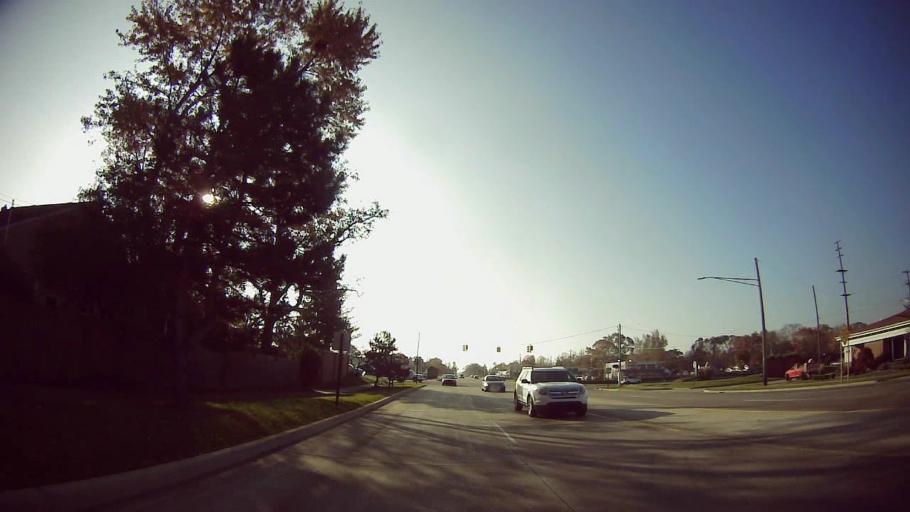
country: US
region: Michigan
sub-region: Oakland County
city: Oak Park
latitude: 42.4756
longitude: -83.1826
